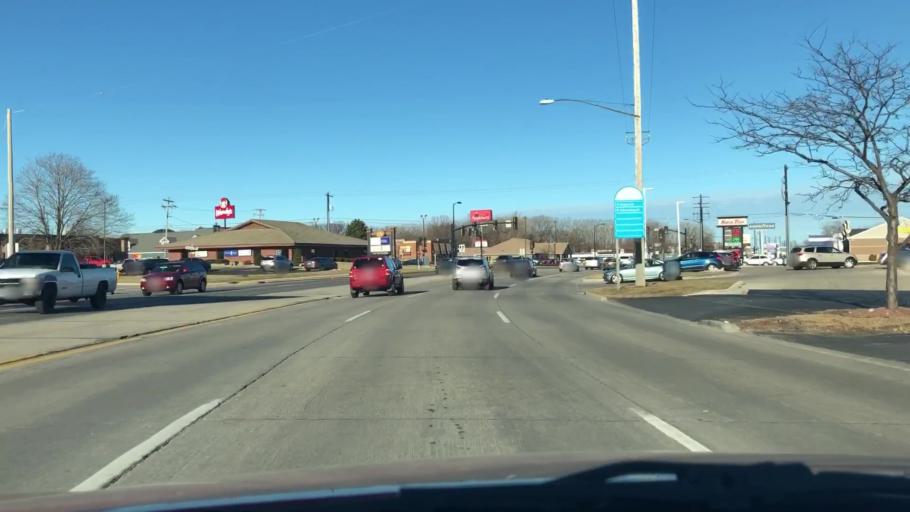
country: US
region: Wisconsin
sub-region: Brown County
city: Ashwaubenon
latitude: 44.4749
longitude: -88.0748
